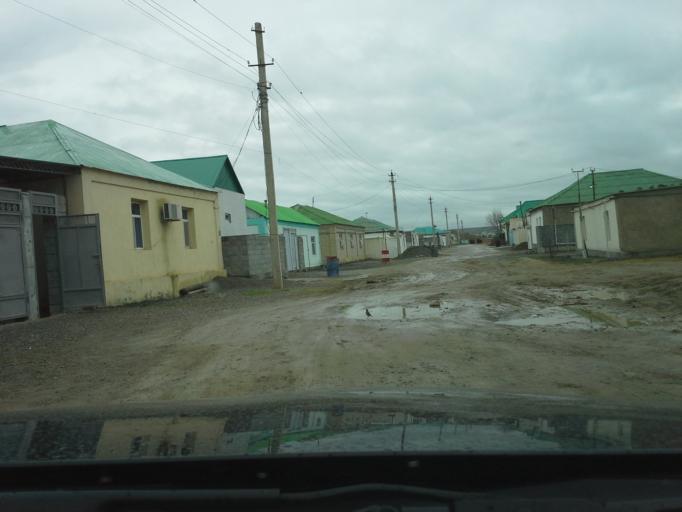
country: TM
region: Ahal
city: Abadan
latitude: 37.9724
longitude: 58.2105
